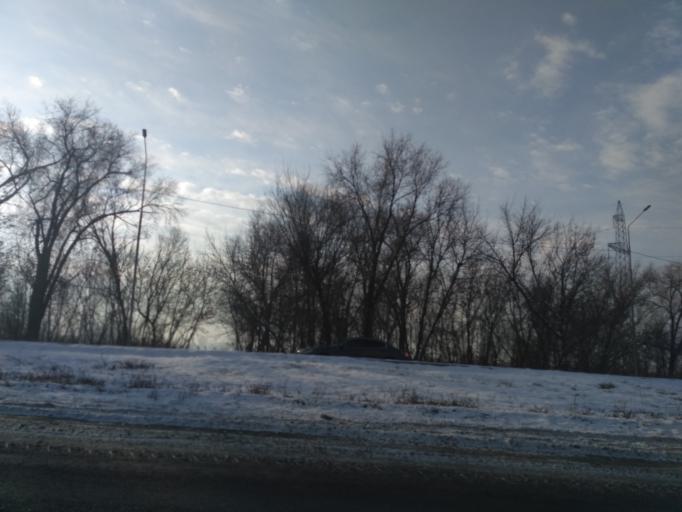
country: KZ
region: Almaty Oblysy
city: Burunday
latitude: 43.2139
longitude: 76.6799
